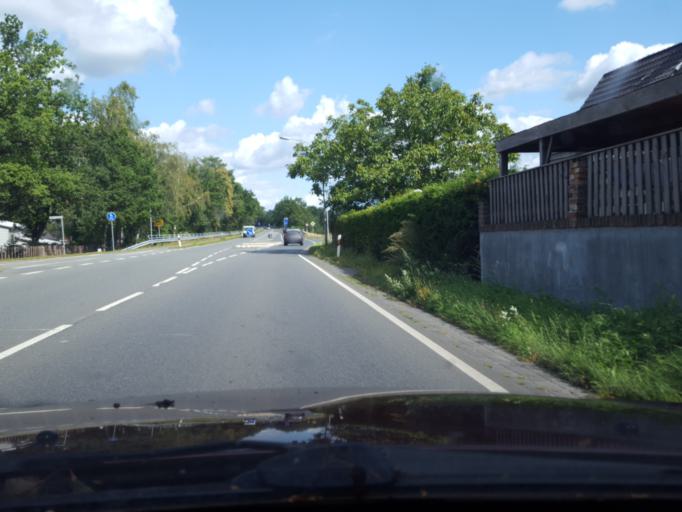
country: DE
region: Lower Saxony
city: Verden
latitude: 52.9543
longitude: 9.2394
